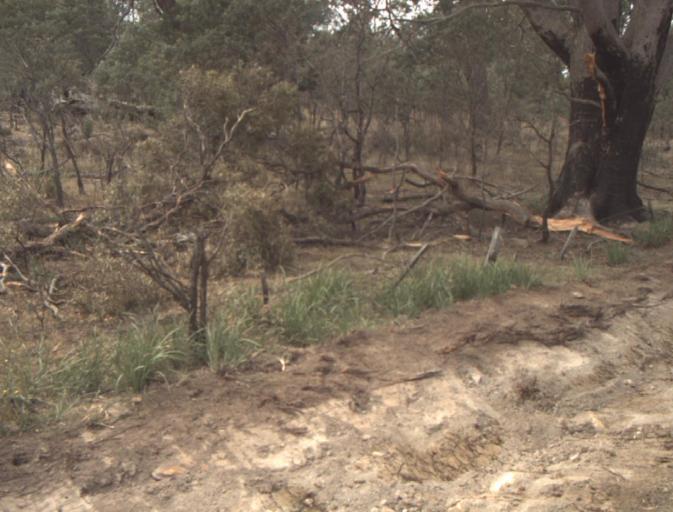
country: AU
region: Tasmania
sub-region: Northern Midlands
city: Evandale
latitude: -41.5110
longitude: 147.3461
